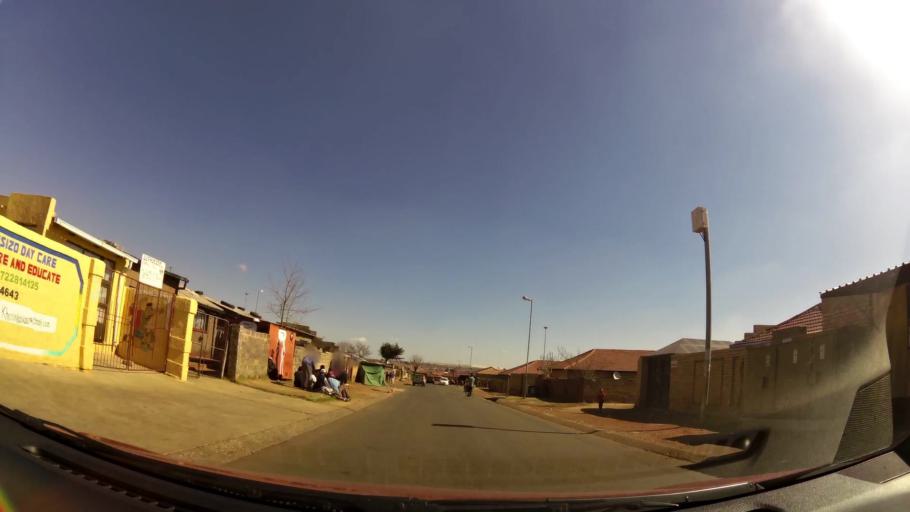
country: ZA
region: Gauteng
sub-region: City of Johannesburg Metropolitan Municipality
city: Soweto
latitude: -26.2373
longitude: 27.8234
